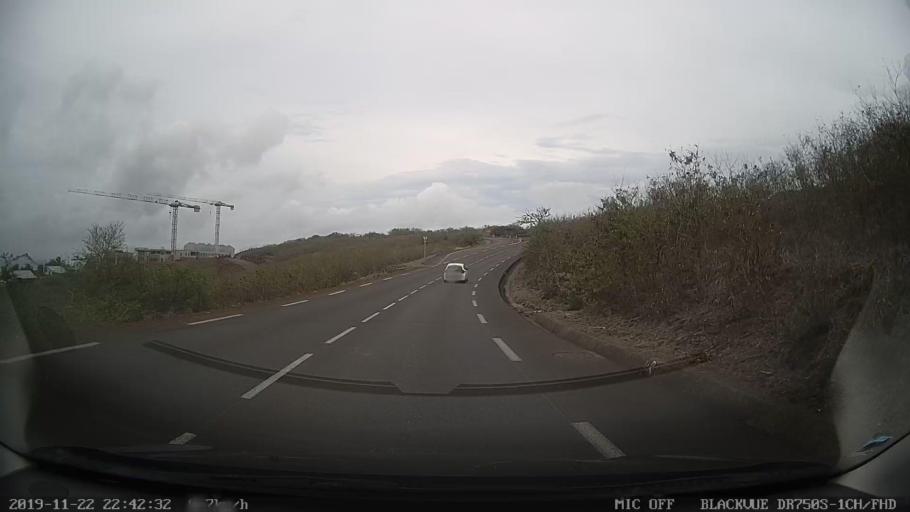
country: RE
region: Reunion
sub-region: Reunion
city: Saint-Paul
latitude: -21.0654
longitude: 55.2324
